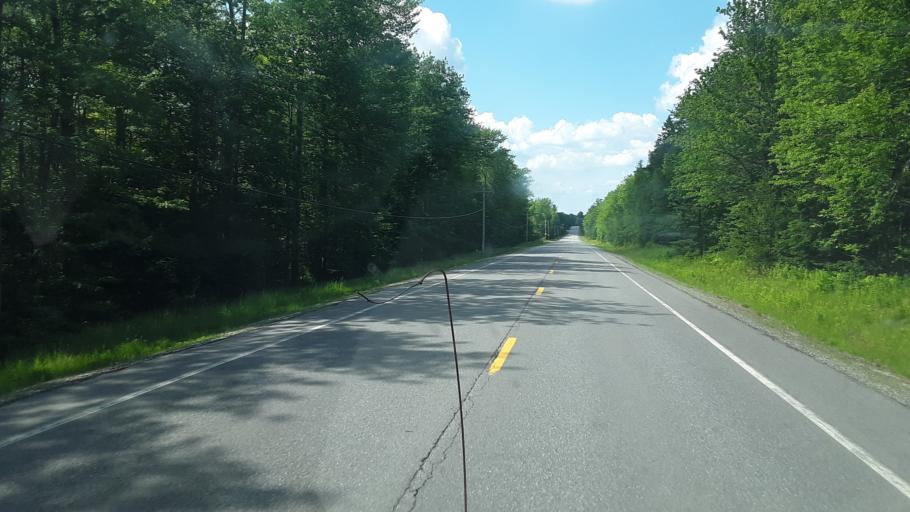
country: US
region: Maine
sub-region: Washington County
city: Machias
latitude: 45.0138
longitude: -67.5555
